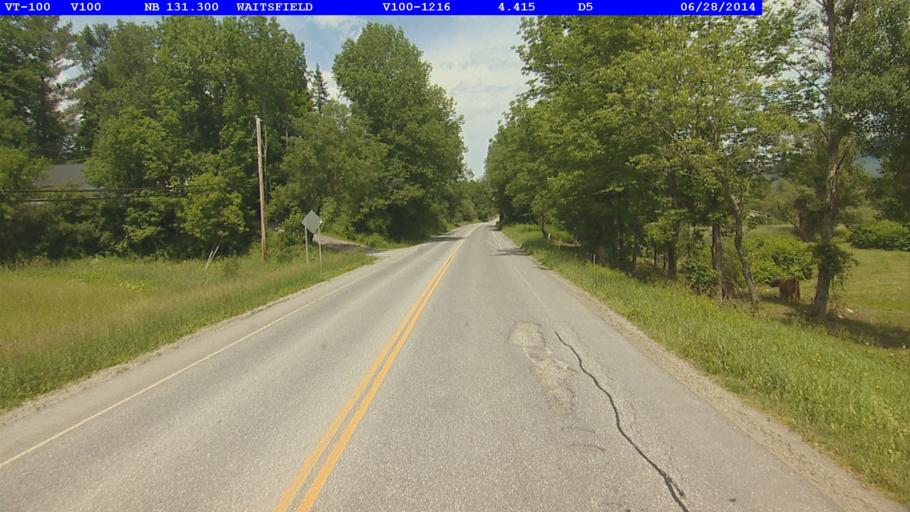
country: US
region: Vermont
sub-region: Washington County
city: Waterbury
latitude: 44.1991
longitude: -72.8154
